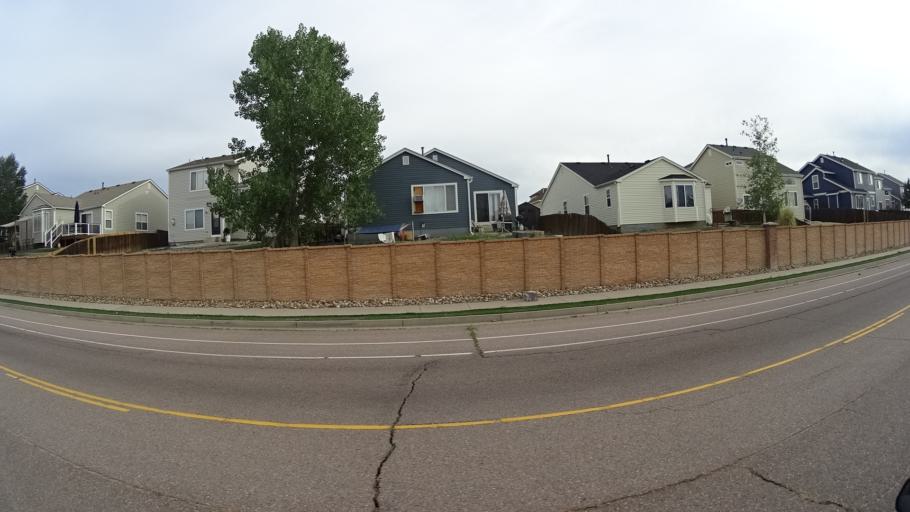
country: US
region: Colorado
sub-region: El Paso County
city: Fountain
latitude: 38.7146
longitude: -104.6890
